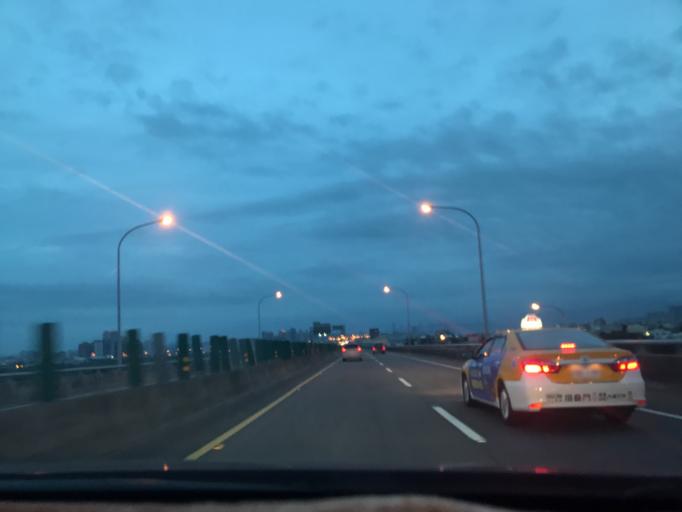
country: TW
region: Taiwan
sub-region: Hsinchu
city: Hsinchu
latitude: 24.8239
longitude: 120.9804
